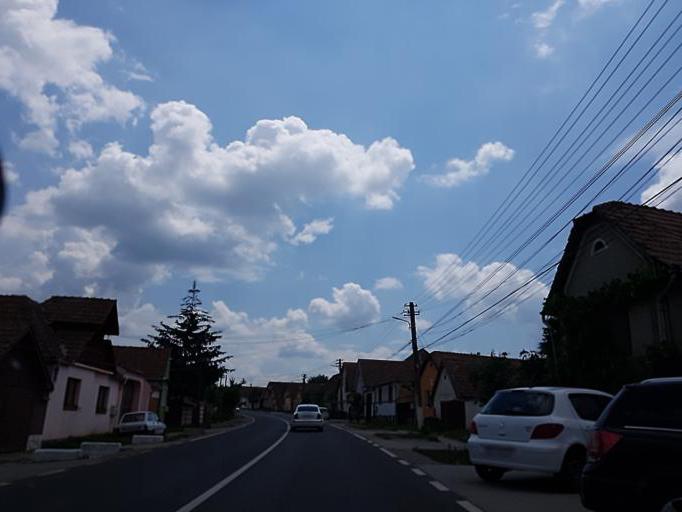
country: RO
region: Sibiu
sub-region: Comuna Slimnic
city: Slimnic
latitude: 45.9125
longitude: 24.1541
